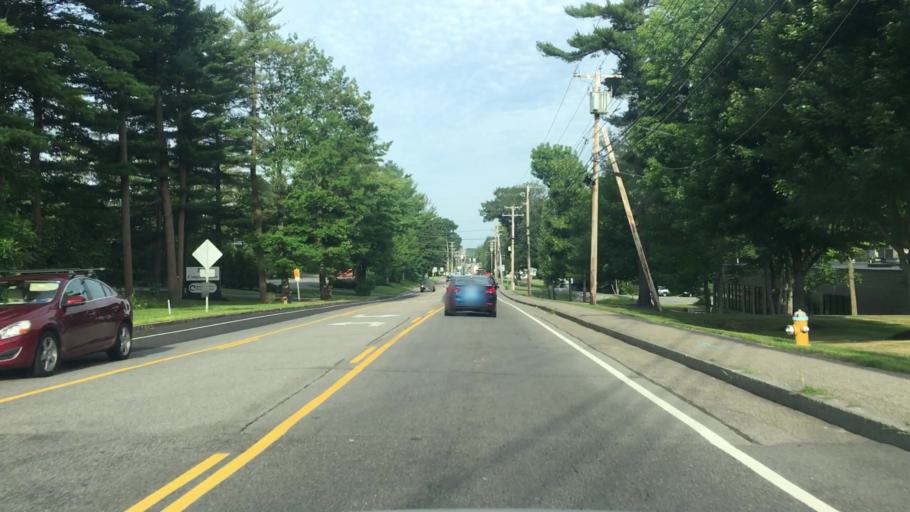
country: US
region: Maine
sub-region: Cumberland County
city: South Portland Gardens
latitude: 43.6509
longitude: -70.3336
